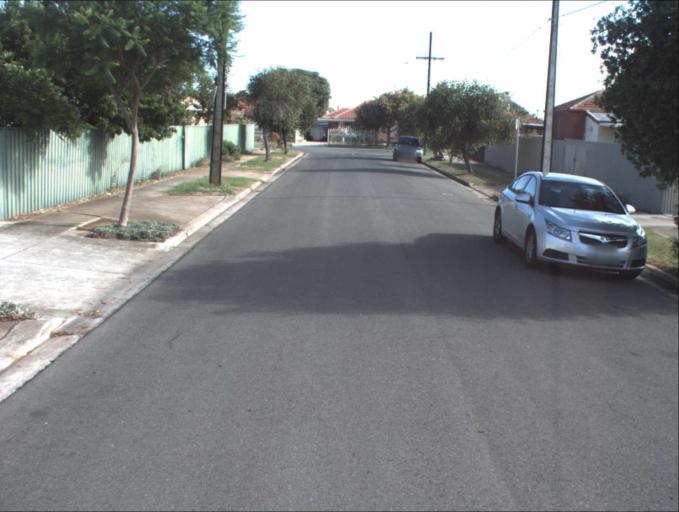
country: AU
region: South Australia
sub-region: Charles Sturt
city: Woodville North
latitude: -34.8646
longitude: 138.5548
